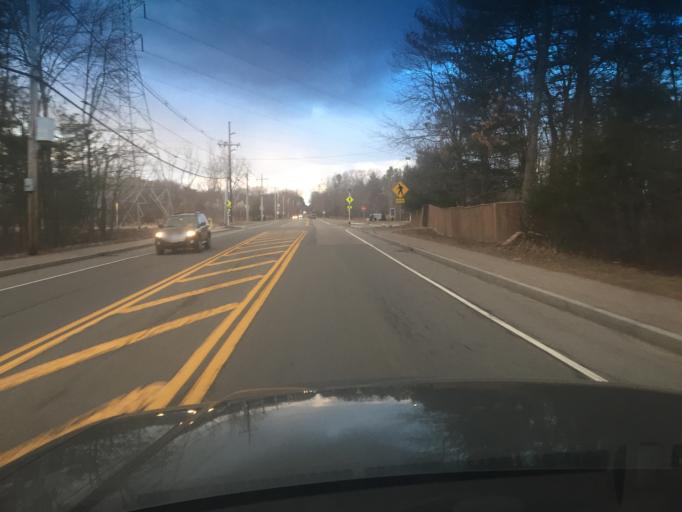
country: US
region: Massachusetts
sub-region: Norfolk County
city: Medway
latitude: 42.1529
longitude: -71.4433
